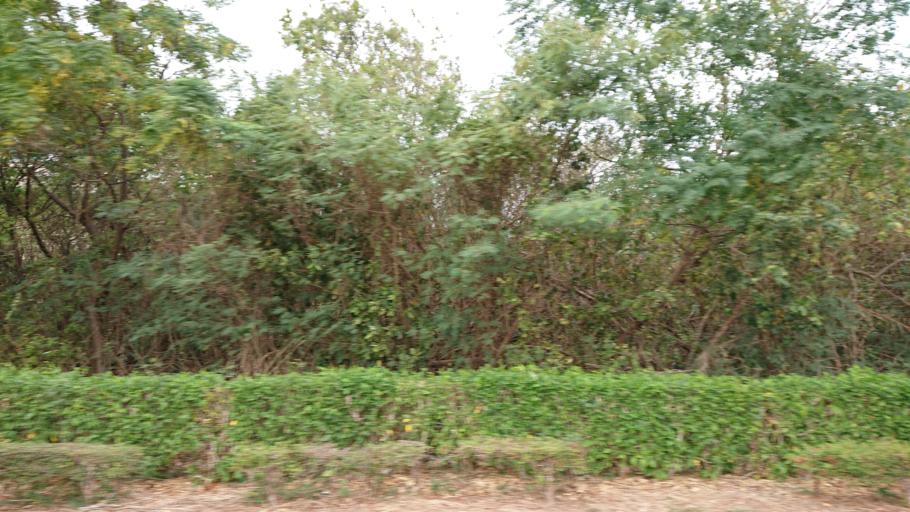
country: TW
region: Fukien
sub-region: Kinmen
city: Jincheng
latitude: 24.4555
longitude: 118.3604
